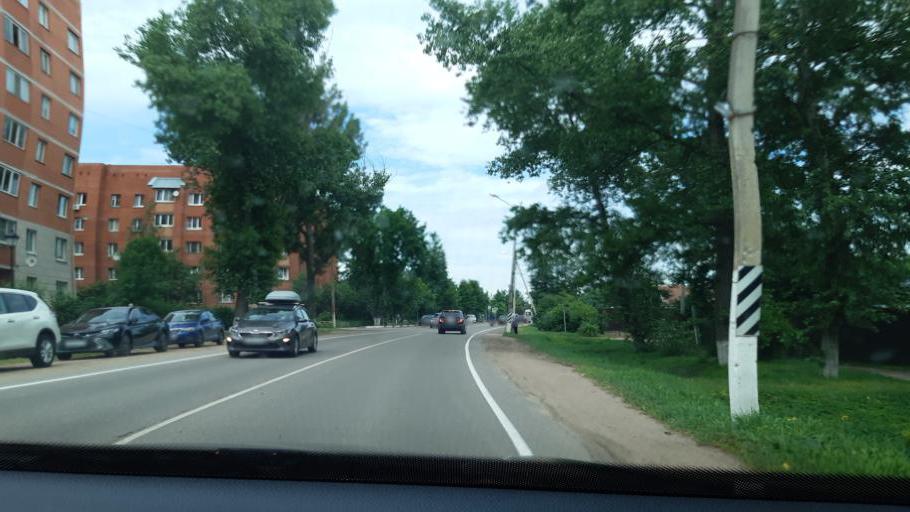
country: RU
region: Moskovskaya
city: Bol'shiye Vyazemy
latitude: 55.6251
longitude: 36.9832
